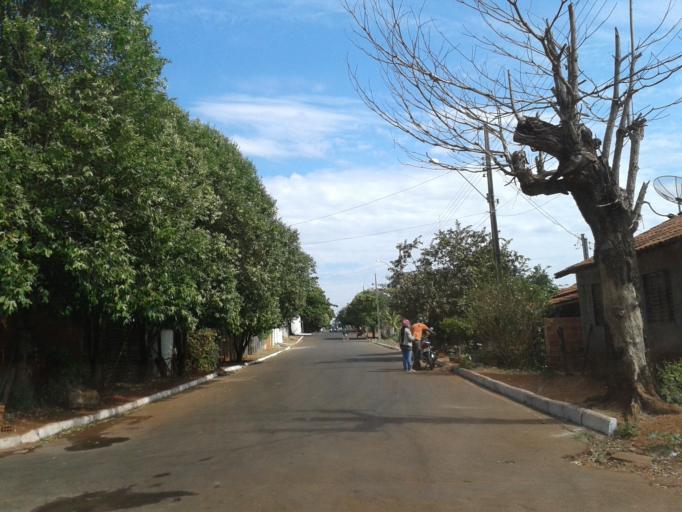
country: BR
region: Minas Gerais
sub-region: Santa Vitoria
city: Santa Vitoria
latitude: -18.8364
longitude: -50.1244
